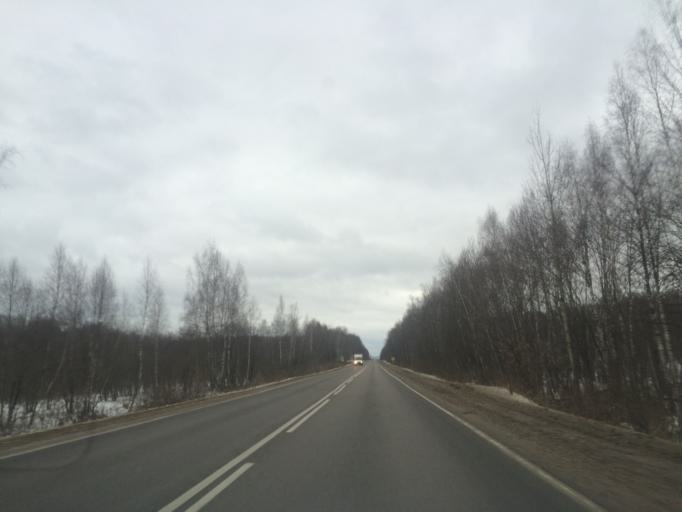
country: RU
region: Tula
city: Krapivna
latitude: 54.1356
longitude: 37.2622
